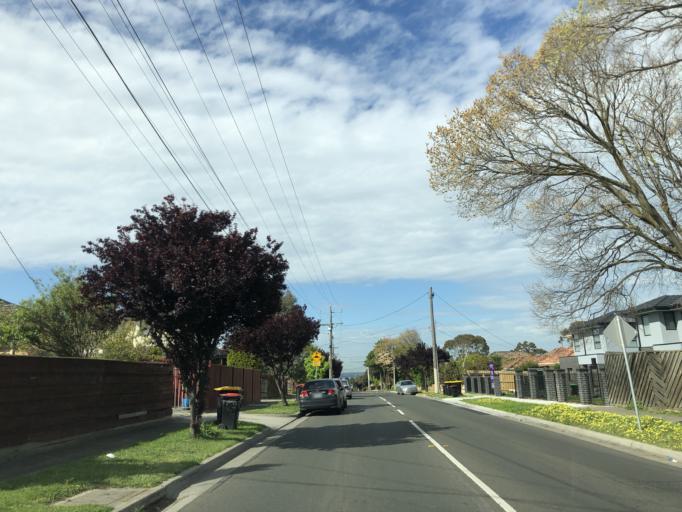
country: AU
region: Victoria
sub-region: Greater Dandenong
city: Dandenong
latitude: -37.9772
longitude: 145.2019
